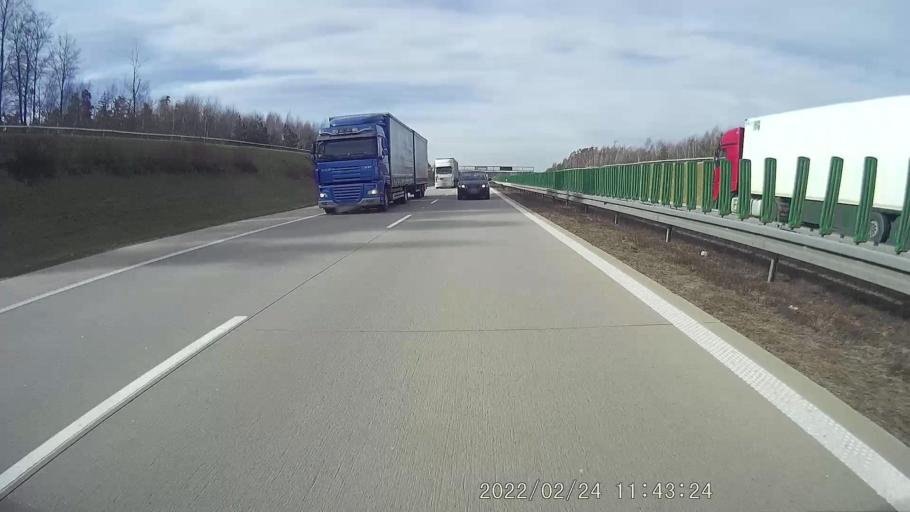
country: PL
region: Lower Silesian Voivodeship
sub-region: Powiat polkowicki
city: Radwanice
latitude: 51.5442
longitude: 15.9136
